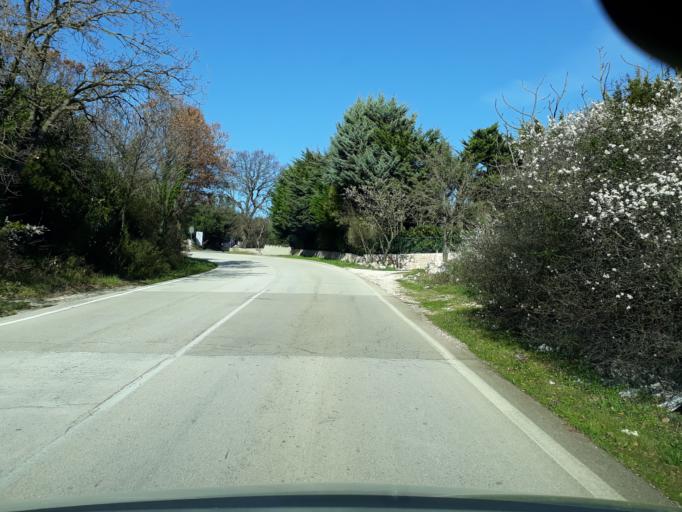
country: IT
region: Apulia
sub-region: Provincia di Bari
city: Cozzana
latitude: 40.8773
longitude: 17.2715
